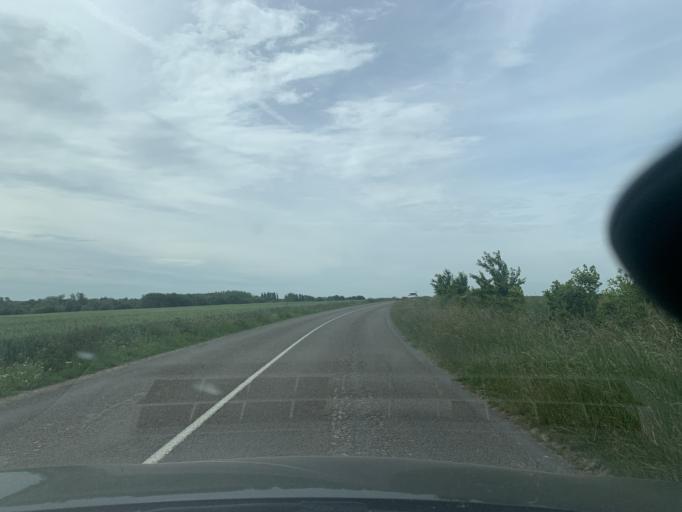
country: FR
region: Nord-Pas-de-Calais
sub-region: Departement du Nord
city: Marcoing
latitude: 50.1327
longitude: 3.1832
